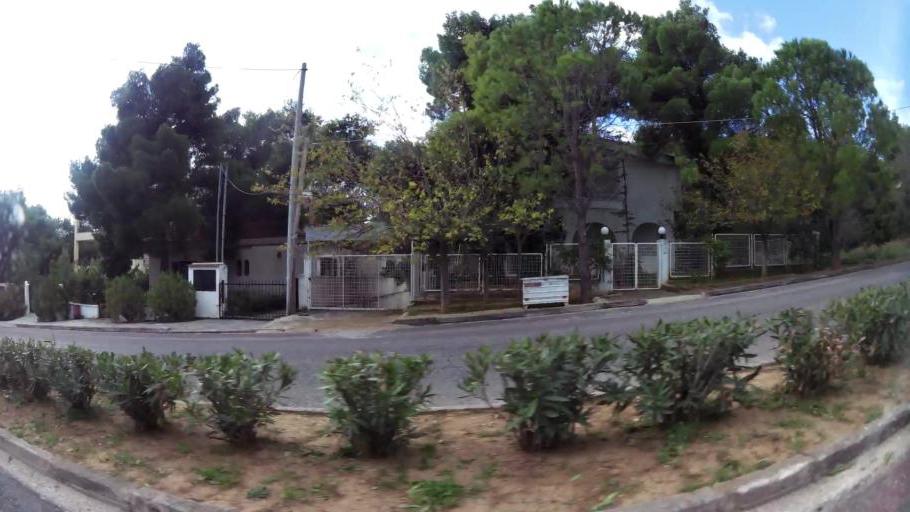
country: GR
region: Attica
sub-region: Nomarchia Anatolikis Attikis
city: Thrakomakedones
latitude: 38.1346
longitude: 23.7600
